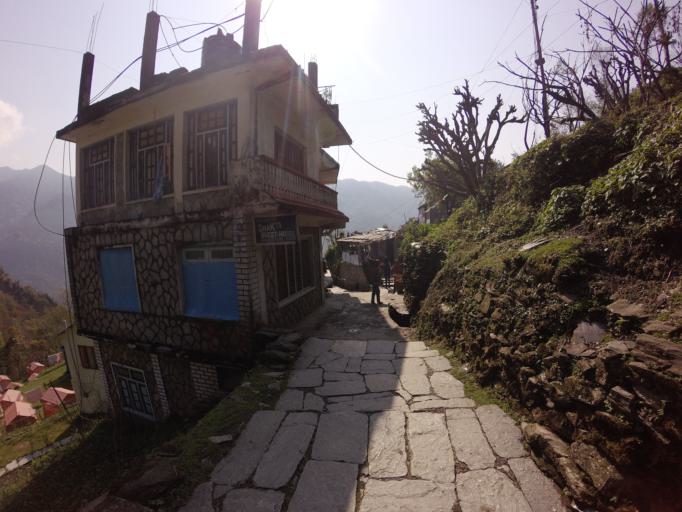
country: NP
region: Western Region
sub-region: Dhawalagiri Zone
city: Chitre
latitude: 28.3732
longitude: 83.8093
